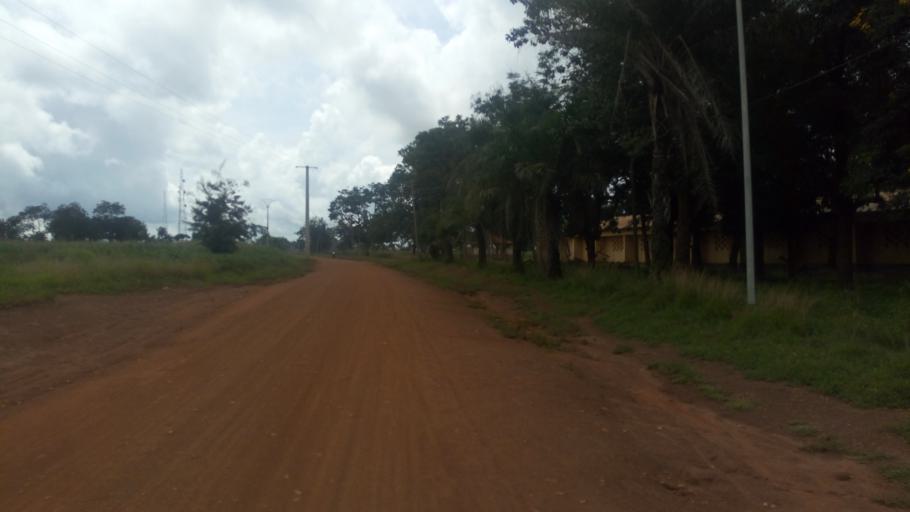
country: TG
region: Centrale
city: Sotouboua
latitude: 8.5572
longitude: 0.9973
